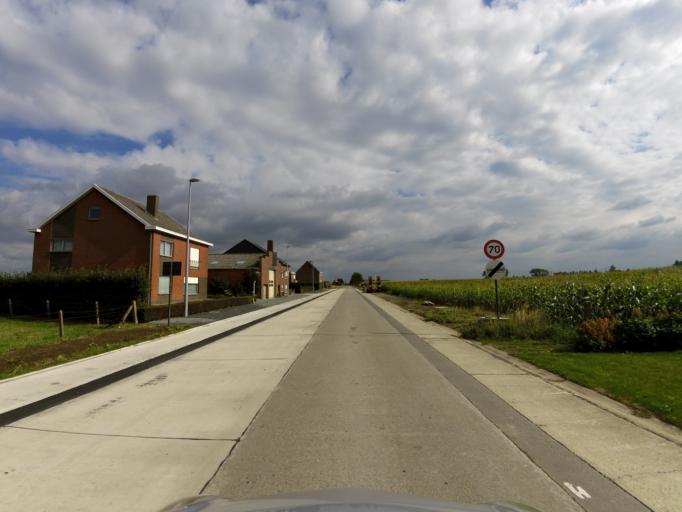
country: BE
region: Flanders
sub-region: Provincie West-Vlaanderen
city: Pittem
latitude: 51.0175
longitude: 3.2691
